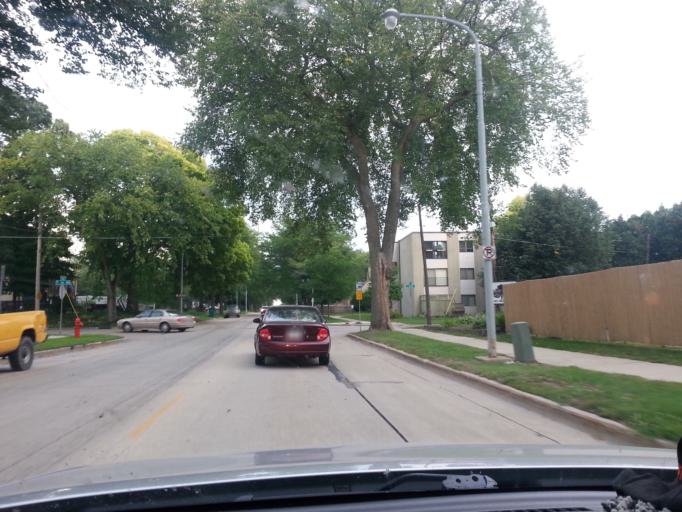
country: US
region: Minnesota
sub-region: Olmsted County
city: Rochester
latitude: 44.0235
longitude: -92.4544
